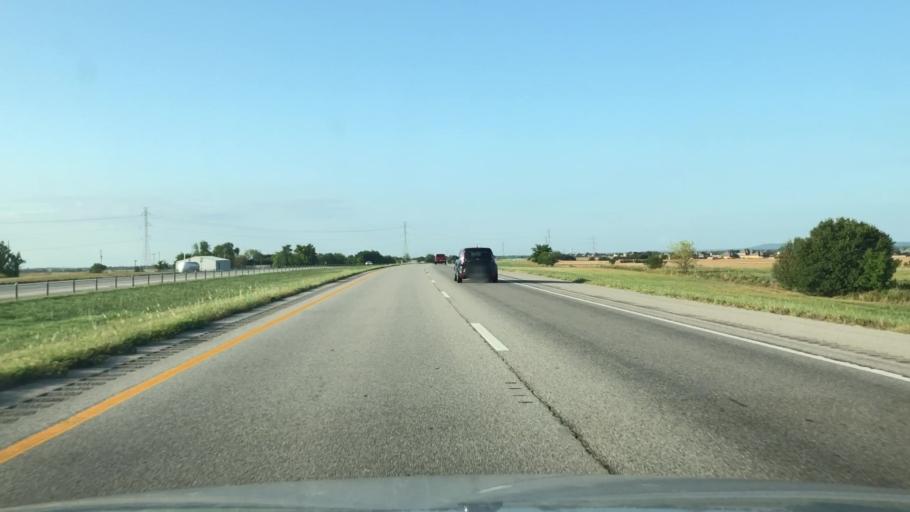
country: US
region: Oklahoma
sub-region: Osage County
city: Skiatook
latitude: 36.3527
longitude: -95.9209
